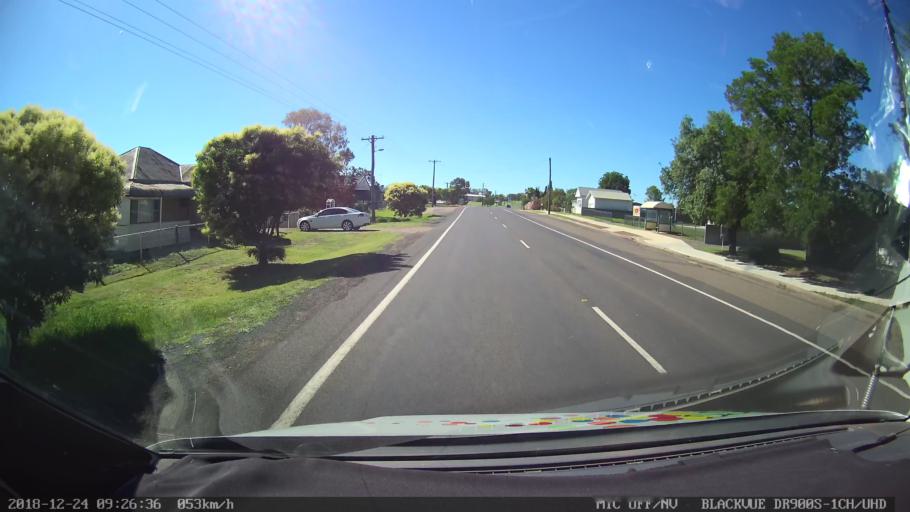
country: AU
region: New South Wales
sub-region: Liverpool Plains
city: Quirindi
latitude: -31.5211
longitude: 150.6775
